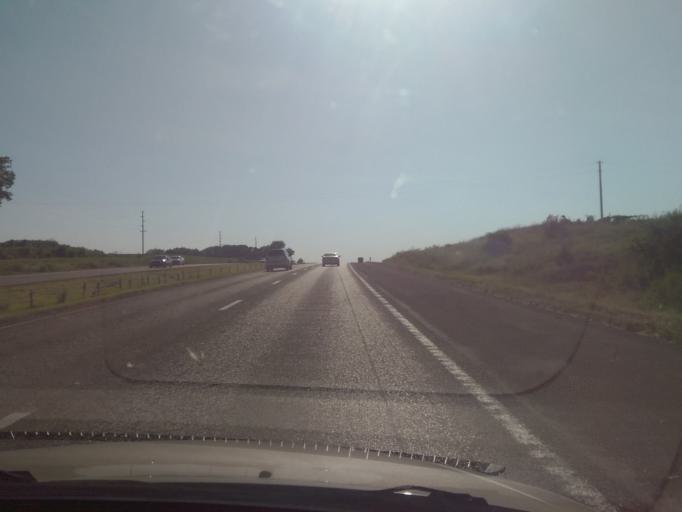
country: US
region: Missouri
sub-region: Lafayette County
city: Concordia
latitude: 38.9916
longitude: -93.6122
